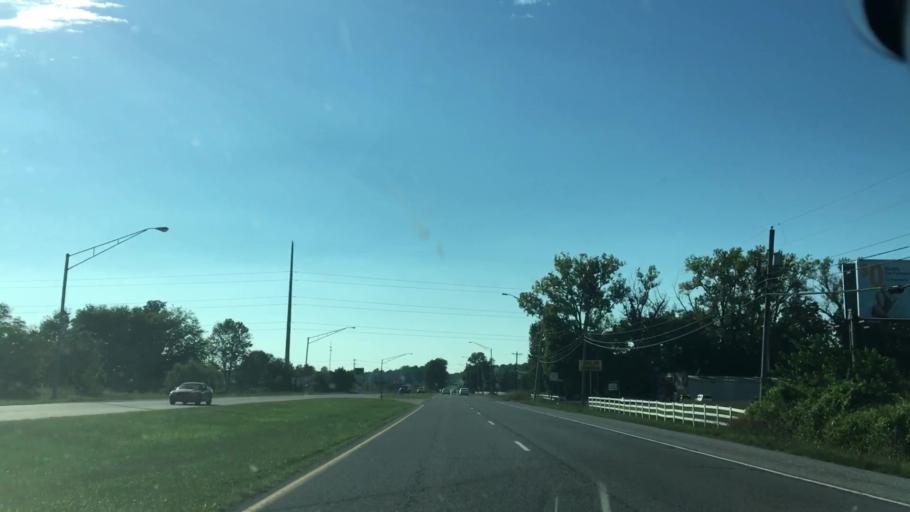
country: US
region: Kentucky
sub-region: Daviess County
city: Owensboro
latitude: 37.7760
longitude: -87.1686
